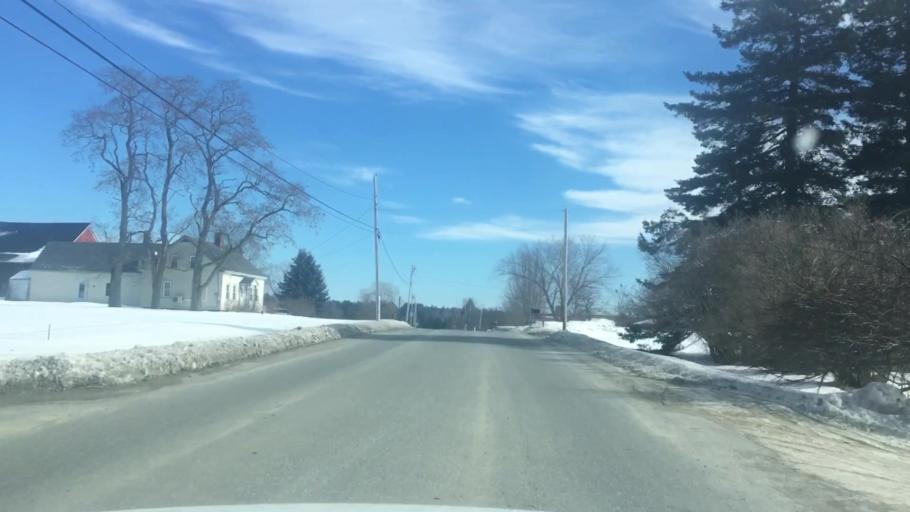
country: US
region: Maine
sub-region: Penobscot County
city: Eddington
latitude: 44.7981
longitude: -68.6751
